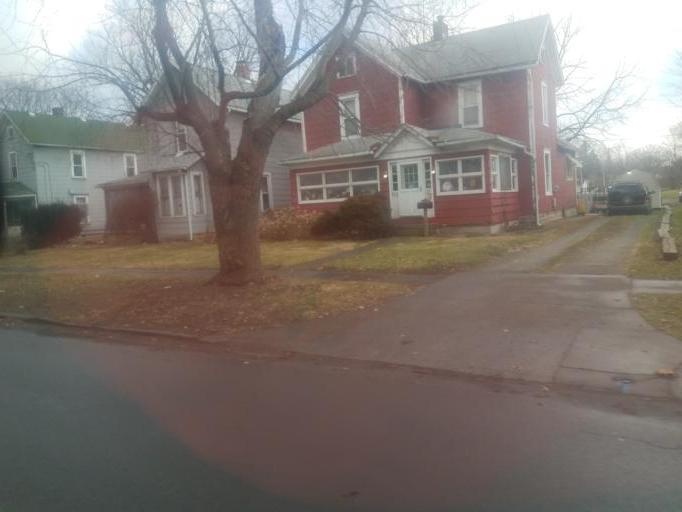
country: US
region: Ohio
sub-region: Marion County
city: Marion
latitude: 40.5913
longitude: -83.1374
